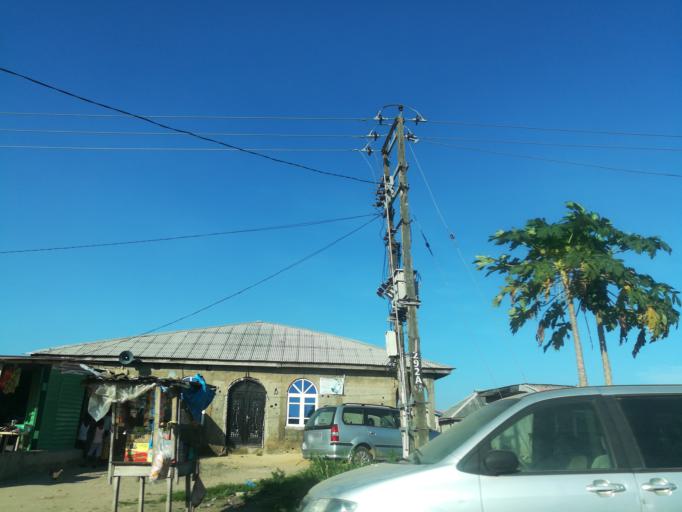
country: NG
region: Lagos
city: Ebute Ikorodu
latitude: 6.5494
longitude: 3.5414
